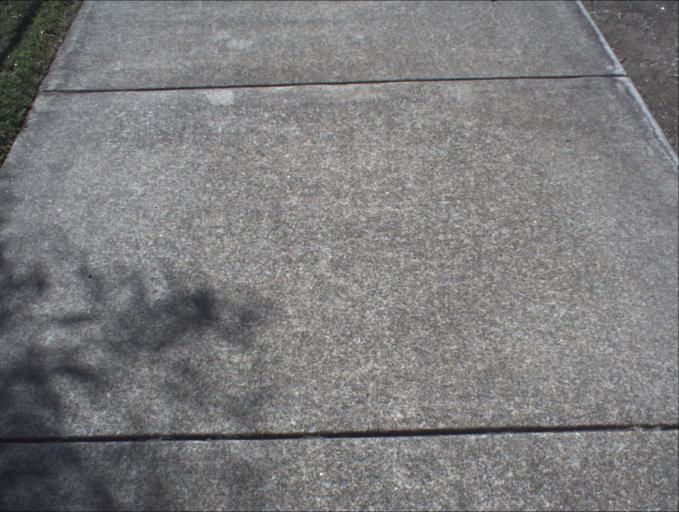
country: AU
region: Queensland
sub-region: Logan
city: Cedar Vale
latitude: -27.8343
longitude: 153.0355
